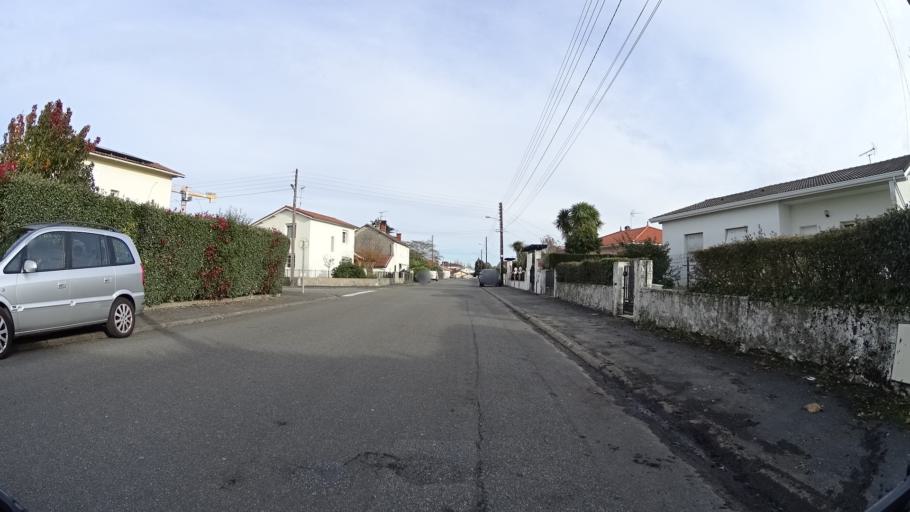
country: FR
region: Aquitaine
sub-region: Departement des Landes
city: Saint-Paul-les-Dax
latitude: 43.7310
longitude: -1.0541
